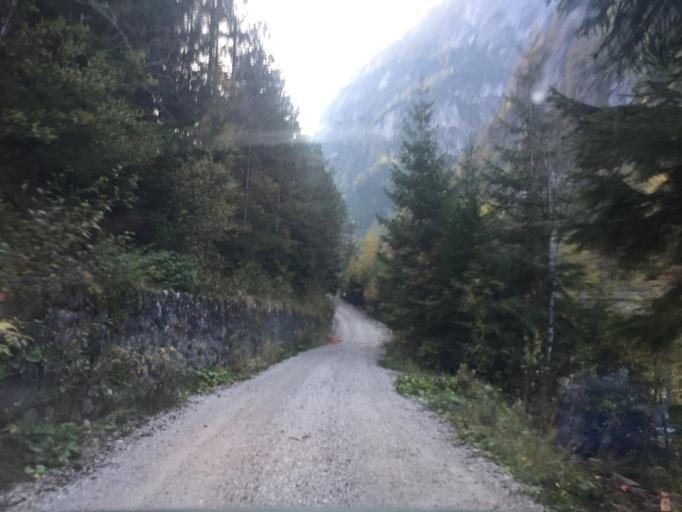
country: IT
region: Veneto
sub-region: Provincia di Belluno
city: San Pietro di Cadore
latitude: 46.5814
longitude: 12.6291
